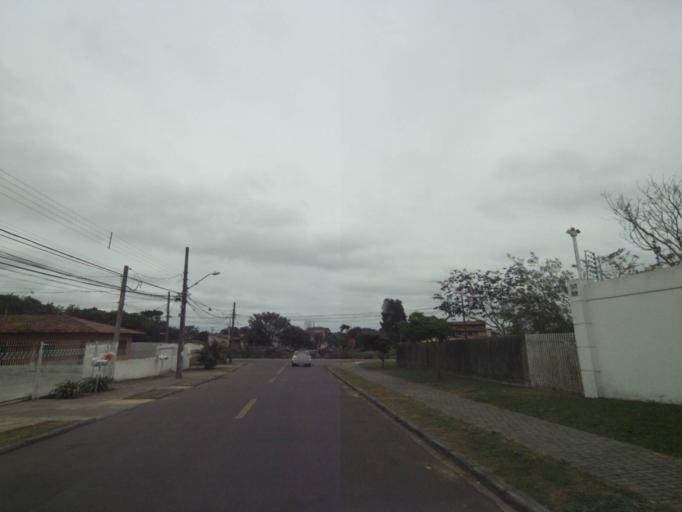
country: BR
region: Parana
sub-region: Sao Jose Dos Pinhais
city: Sao Jose dos Pinhais
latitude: -25.4828
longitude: -49.2363
